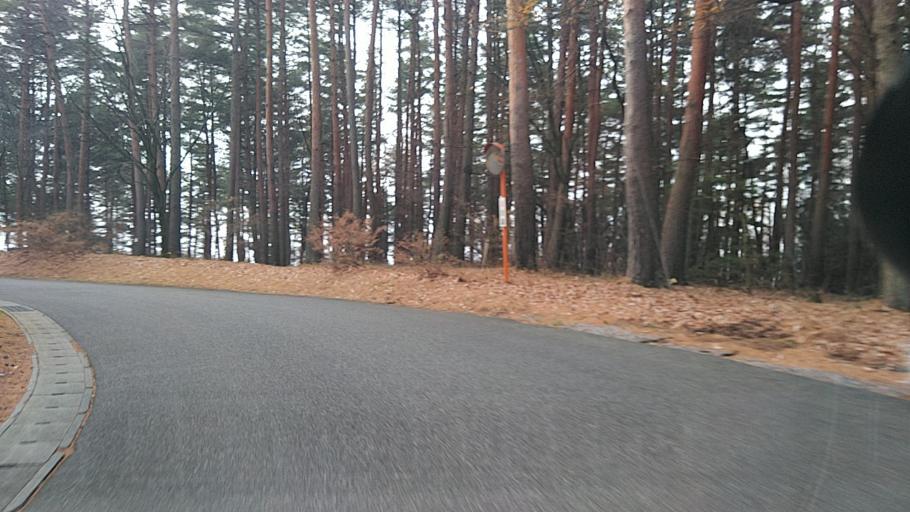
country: JP
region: Nagano
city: Shiojiri
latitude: 36.1444
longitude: 137.9917
